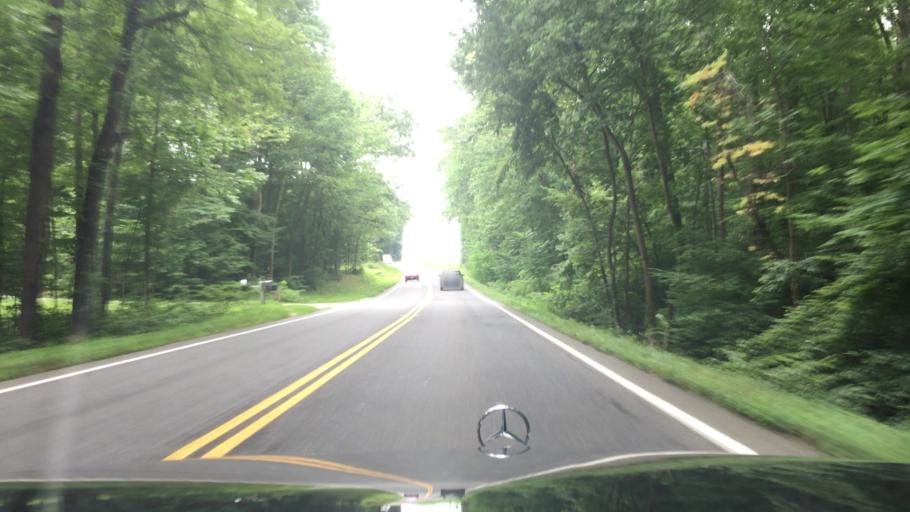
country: US
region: Virginia
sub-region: Nottoway County
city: Crewe
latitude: 37.2737
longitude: -78.1688
